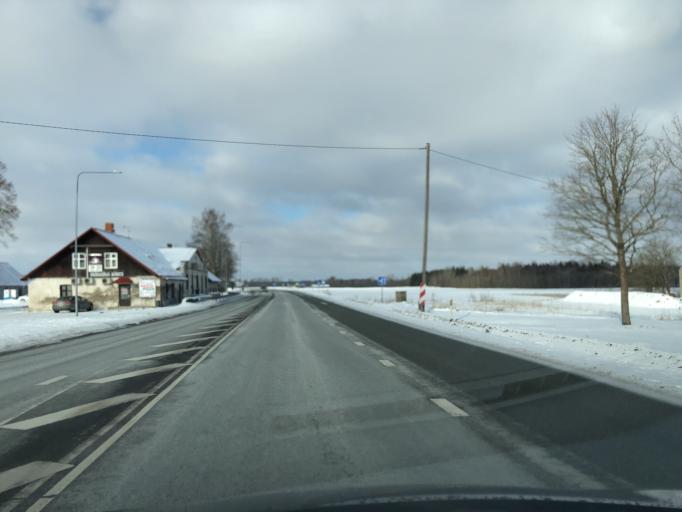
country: EE
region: Jaervamaa
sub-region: Paide linn
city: Paide
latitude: 58.8793
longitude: 25.6922
